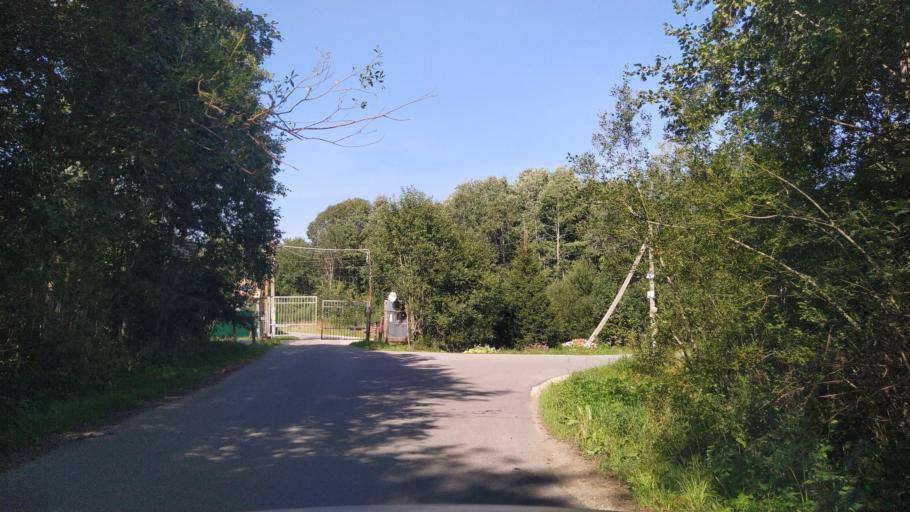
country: RU
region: Leningrad
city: Rozhdestveno
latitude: 59.2660
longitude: 30.0240
